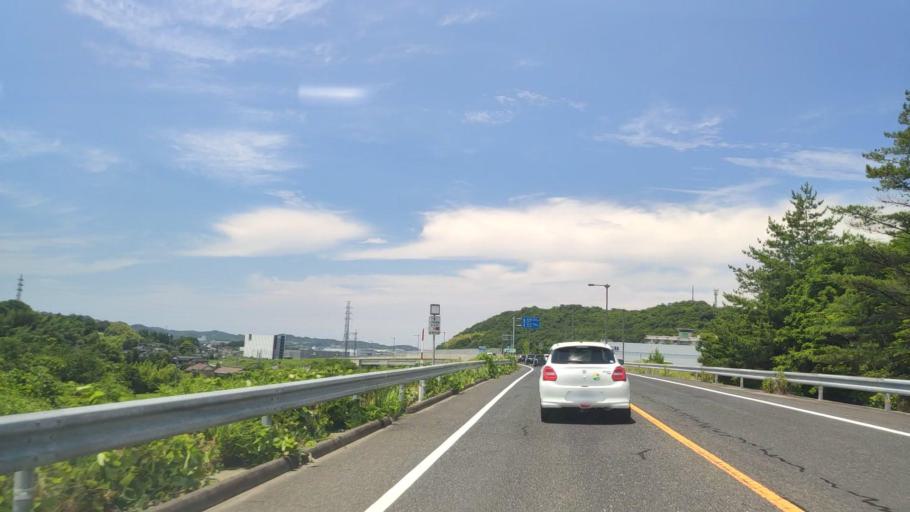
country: JP
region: Tottori
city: Tottori
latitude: 35.4469
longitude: 134.2555
